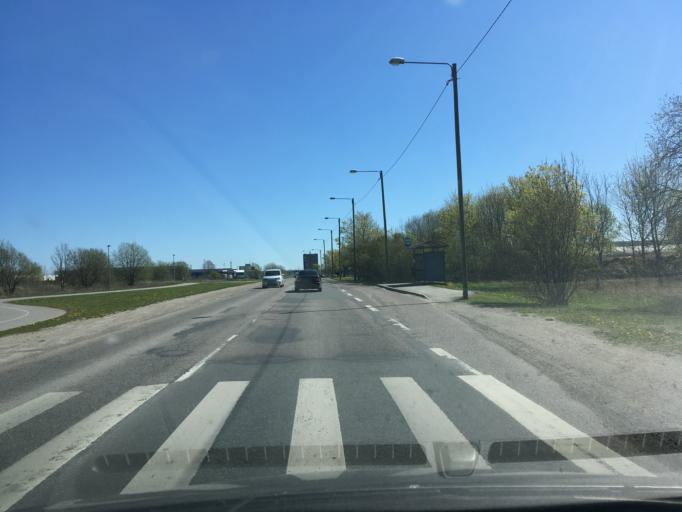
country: EE
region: Harju
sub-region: Joelaehtme vald
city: Loo
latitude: 59.4601
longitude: 24.9276
